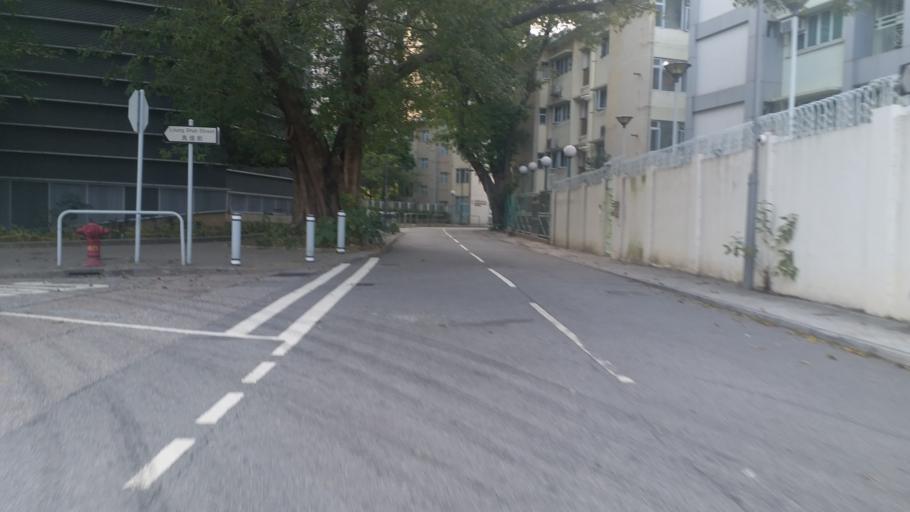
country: HK
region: Tuen Mun
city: Tuen Mun
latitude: 22.4091
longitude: 113.9699
